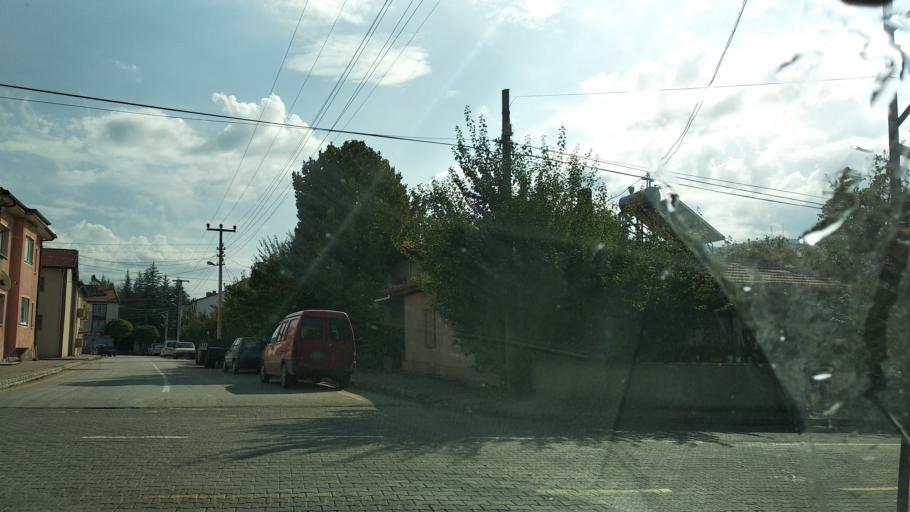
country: TR
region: Bolu
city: Seben
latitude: 40.4100
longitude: 31.5713
